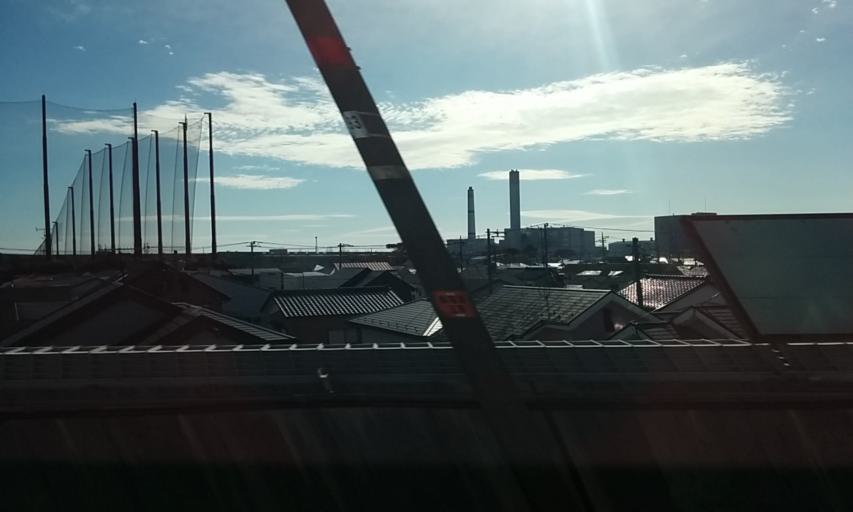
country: JP
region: Kanagawa
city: Atsugi
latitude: 35.3888
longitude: 139.3679
